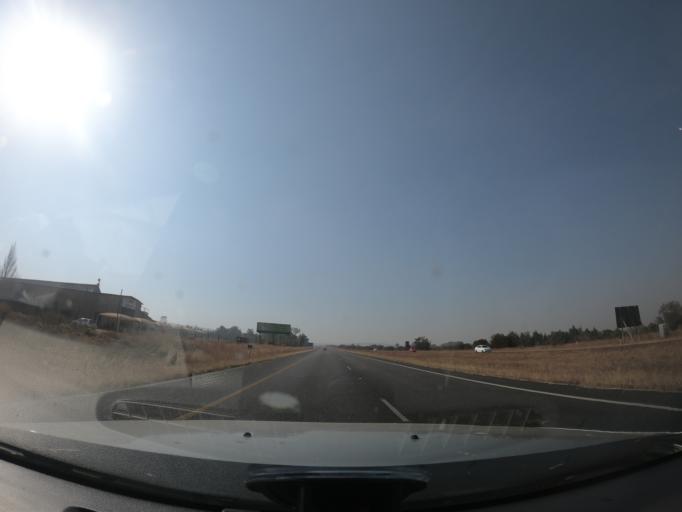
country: ZA
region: Gauteng
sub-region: City of Tshwane Metropolitan Municipality
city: Cullinan
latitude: -25.7705
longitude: 28.4164
